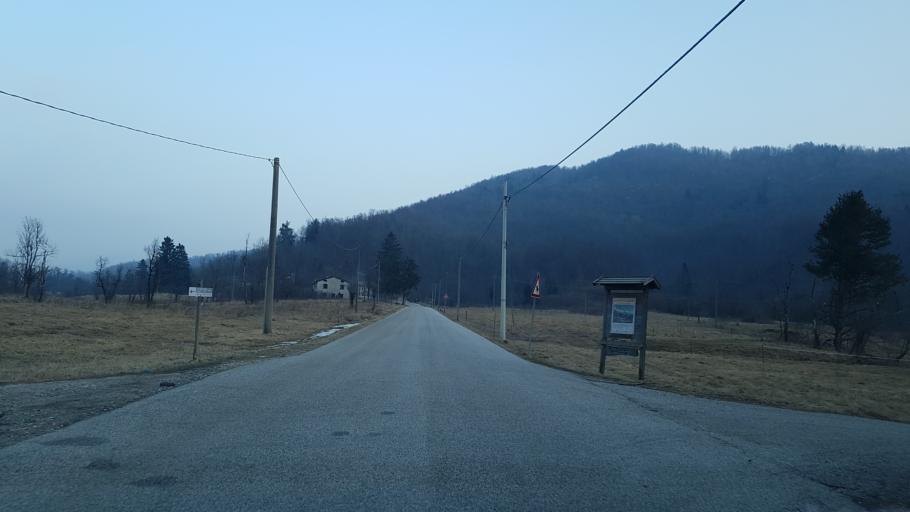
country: IT
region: Friuli Venezia Giulia
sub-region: Provincia di Udine
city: Taipana
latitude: 46.2555
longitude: 13.3634
